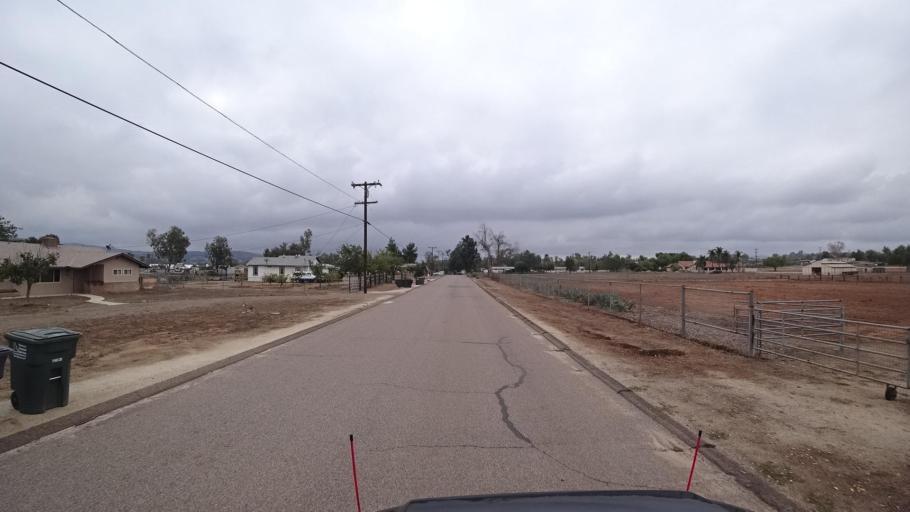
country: US
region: California
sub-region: San Diego County
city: Ramona
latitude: 33.0677
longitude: -116.8632
